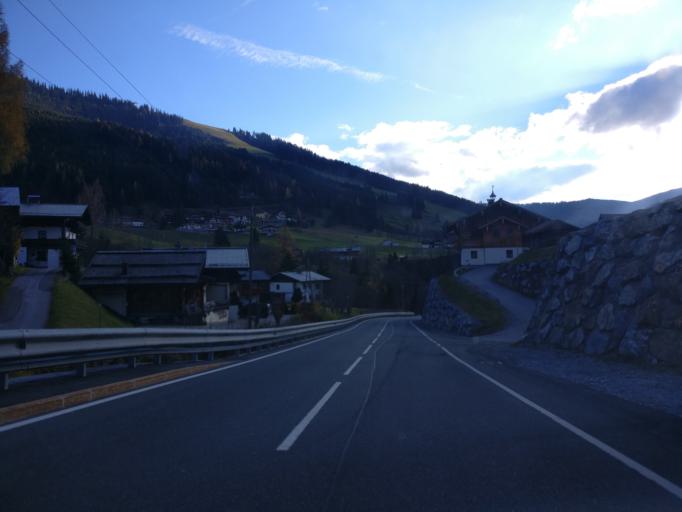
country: AT
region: Salzburg
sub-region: Politischer Bezirk Zell am See
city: Dienten am Hochkonig
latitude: 47.3903
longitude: 13.0156
